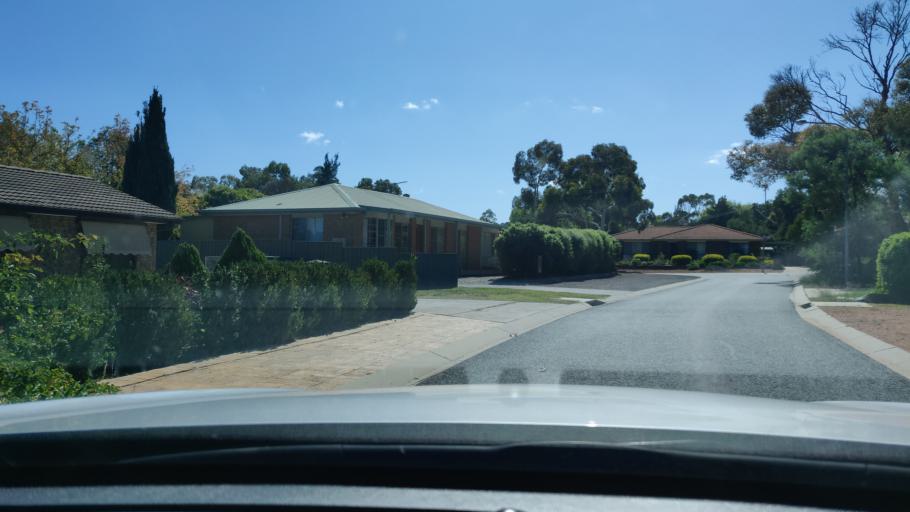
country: AU
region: Australian Capital Territory
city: Macarthur
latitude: -35.4420
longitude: 149.0981
